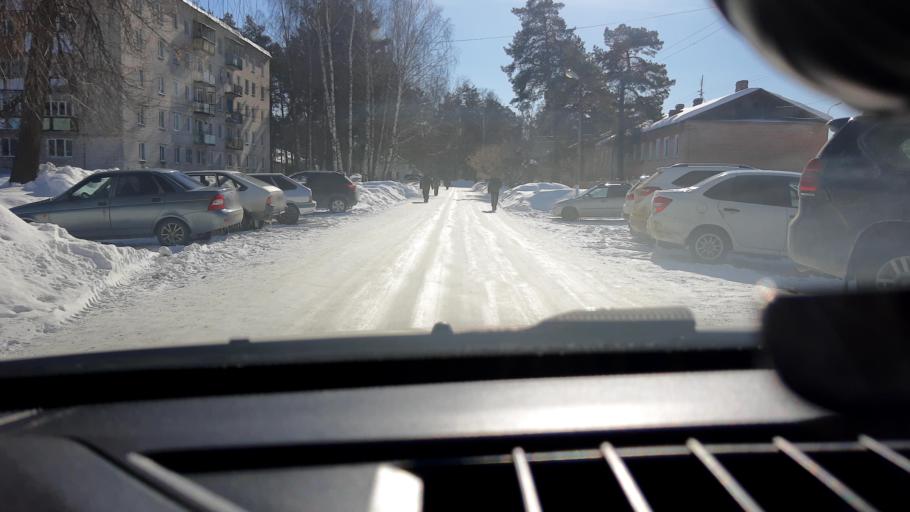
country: RU
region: Nizjnij Novgorod
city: Yuganets
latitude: 56.2521
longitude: 43.2328
